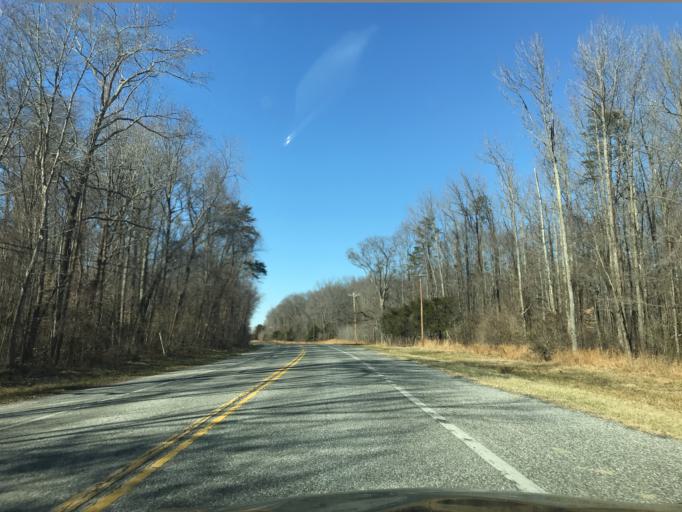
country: US
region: Virginia
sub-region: Fairfax County
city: Mount Vernon
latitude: 38.6755
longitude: -77.0895
